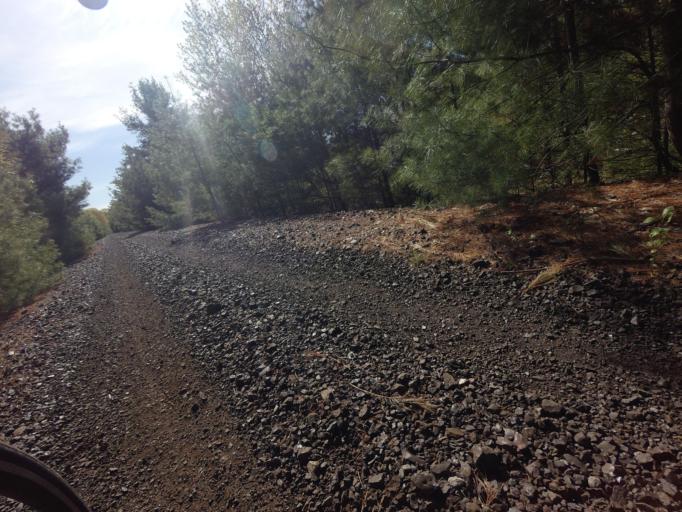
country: CA
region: Ontario
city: Arnprior
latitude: 45.4710
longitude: -76.2945
